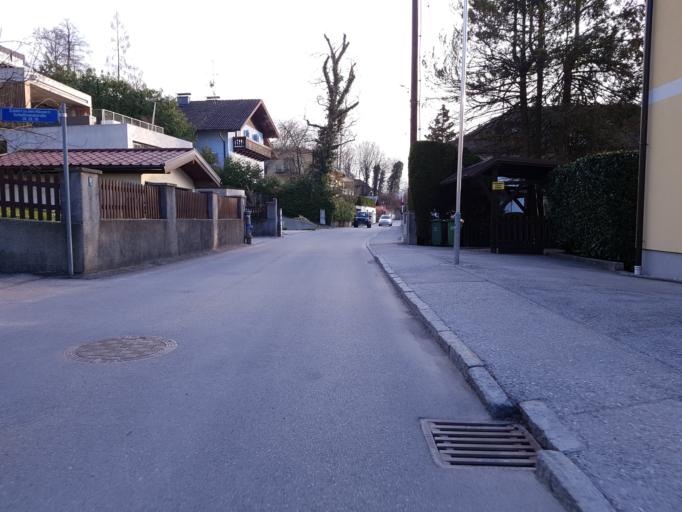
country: AT
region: Salzburg
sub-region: Politischer Bezirk Salzburg-Umgebung
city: Elsbethen
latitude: 47.7748
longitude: 13.0895
